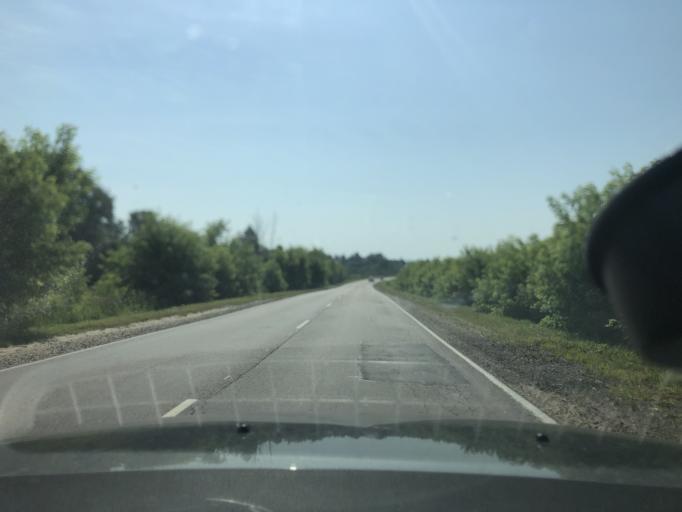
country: RU
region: Tula
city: Dubna
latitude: 54.1106
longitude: 37.0998
